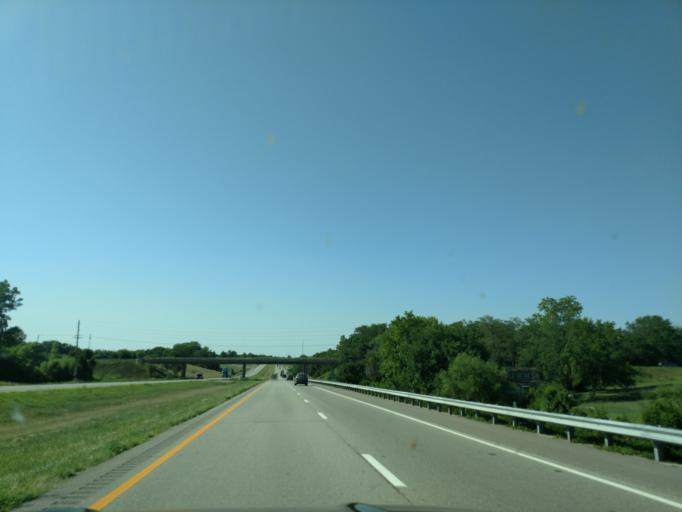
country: US
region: Missouri
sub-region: Andrew County
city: Country Club Village
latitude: 39.8051
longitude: -94.8003
